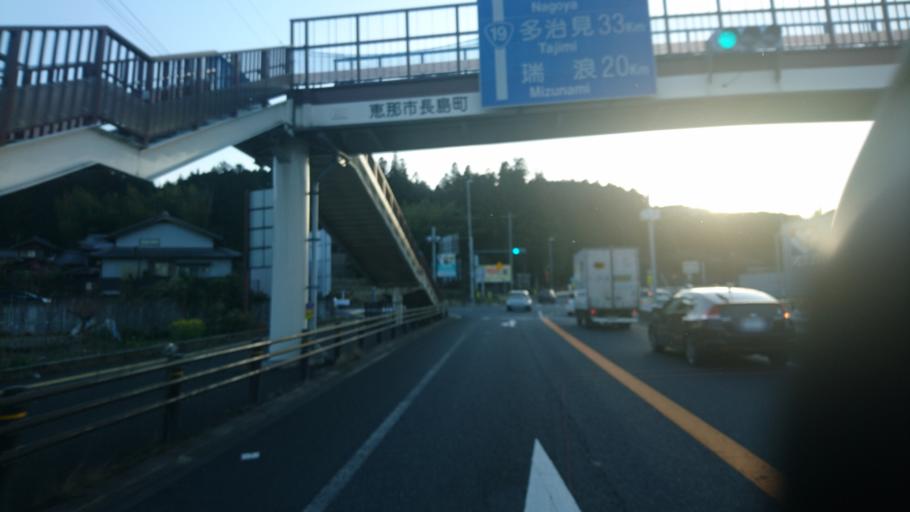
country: JP
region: Gifu
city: Nakatsugawa
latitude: 35.4461
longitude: 137.4111
